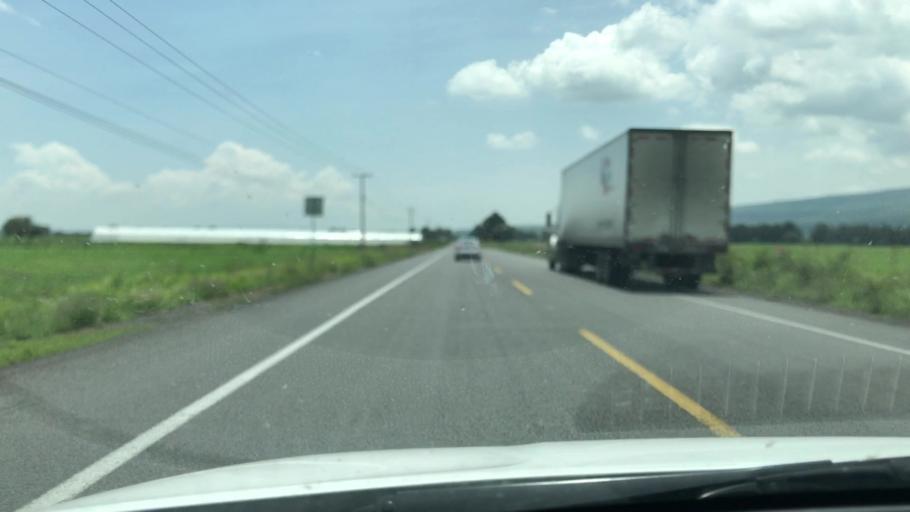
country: MX
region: Michoacan
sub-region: Yurecuaro
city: Yurecuaro
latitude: 20.3384
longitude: -102.1862
